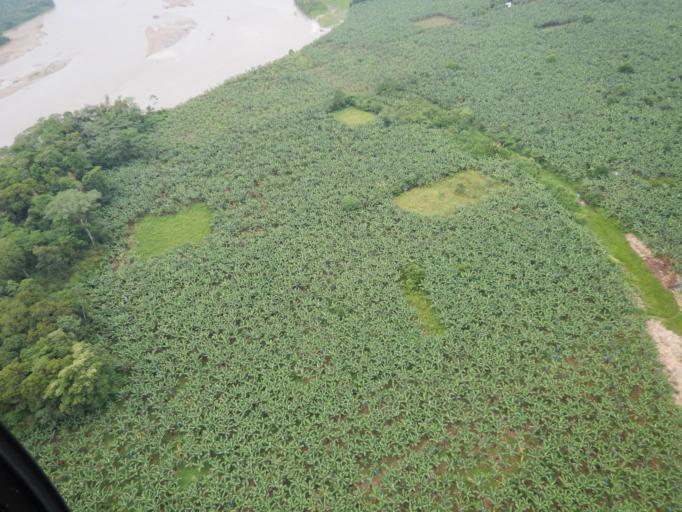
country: BO
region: Cochabamba
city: Chimore
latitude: -17.1299
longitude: -64.8212
